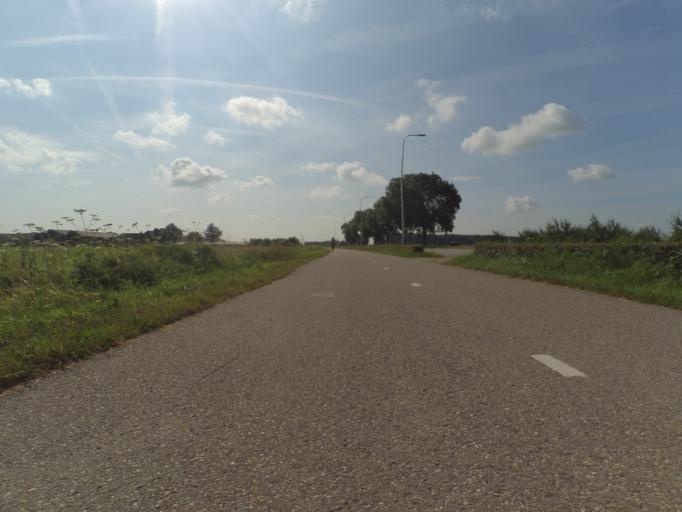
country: NL
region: Utrecht
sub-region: Gemeente Utrechtse Heuvelrug
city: Driebergen-Rijsenburg
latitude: 52.0362
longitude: 5.2358
